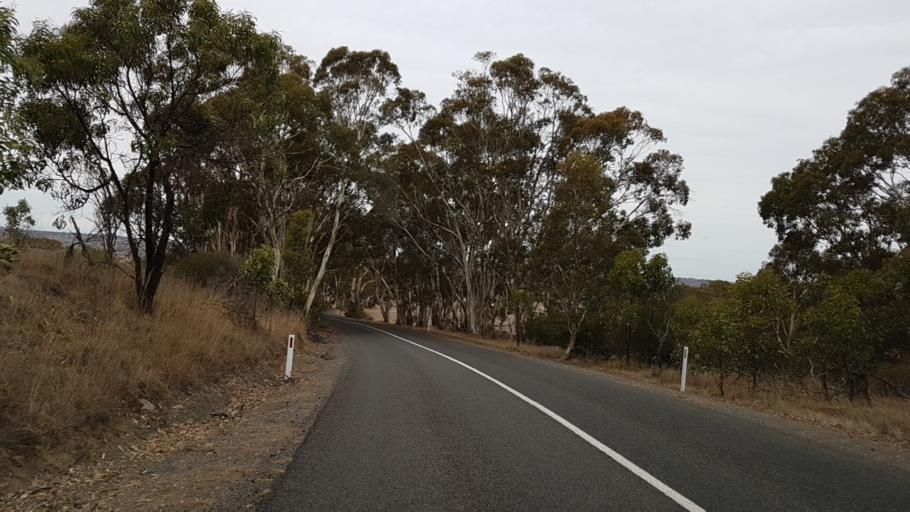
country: AU
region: South Australia
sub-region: Mount Barker
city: Nairne
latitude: -34.9859
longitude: 138.9881
